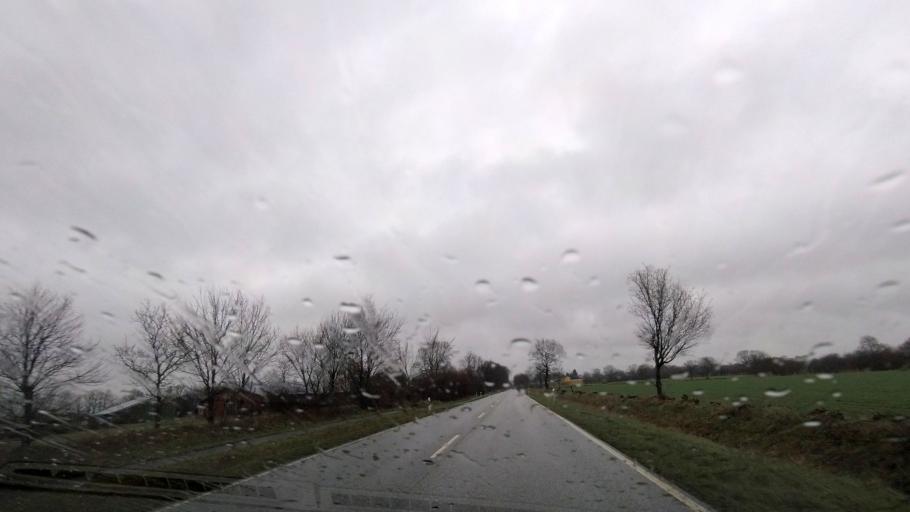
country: DE
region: Schleswig-Holstein
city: Wanderup
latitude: 54.6813
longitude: 9.3190
